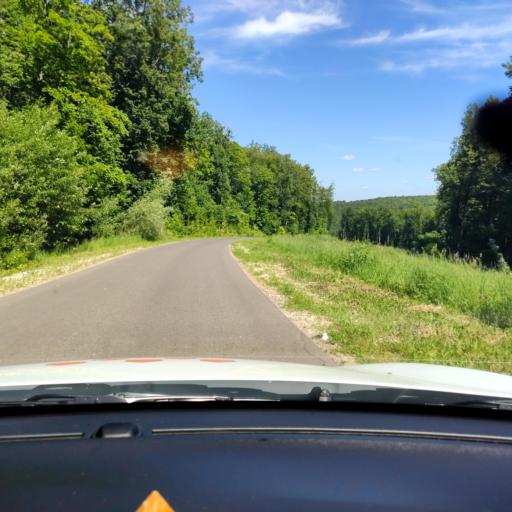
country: RU
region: Tatarstan
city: Sviyazhsk
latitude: 55.7754
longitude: 48.7802
